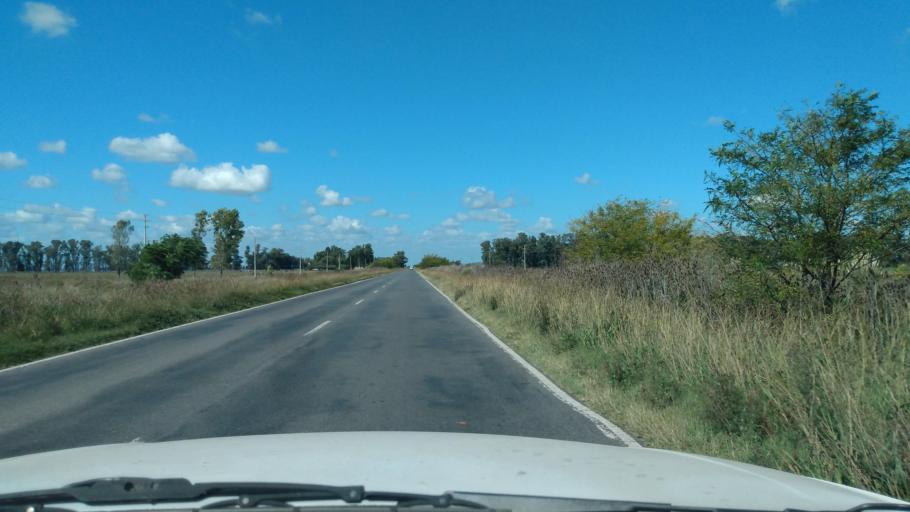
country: AR
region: Buenos Aires
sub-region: Partido de Mercedes
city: Mercedes
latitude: -34.7342
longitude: -59.3883
